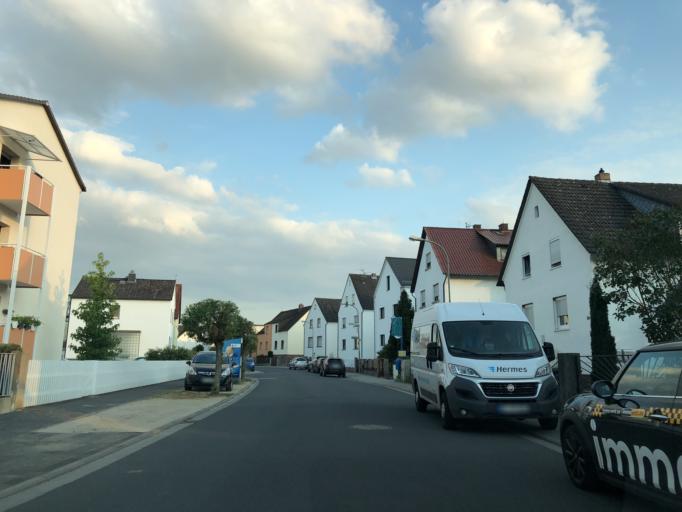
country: DE
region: Hesse
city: Obertshausen
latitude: 50.0954
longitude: 8.8518
